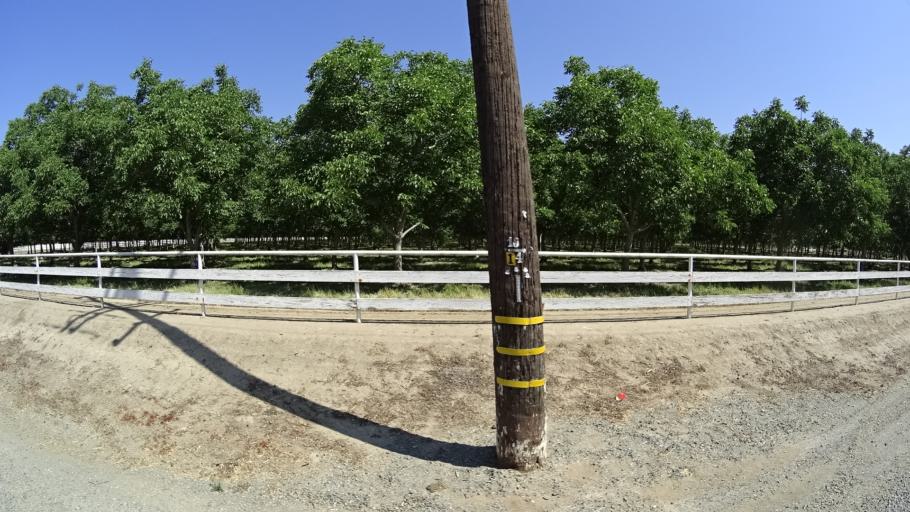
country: US
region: California
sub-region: Kings County
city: Lucerne
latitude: 36.3719
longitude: -119.6471
